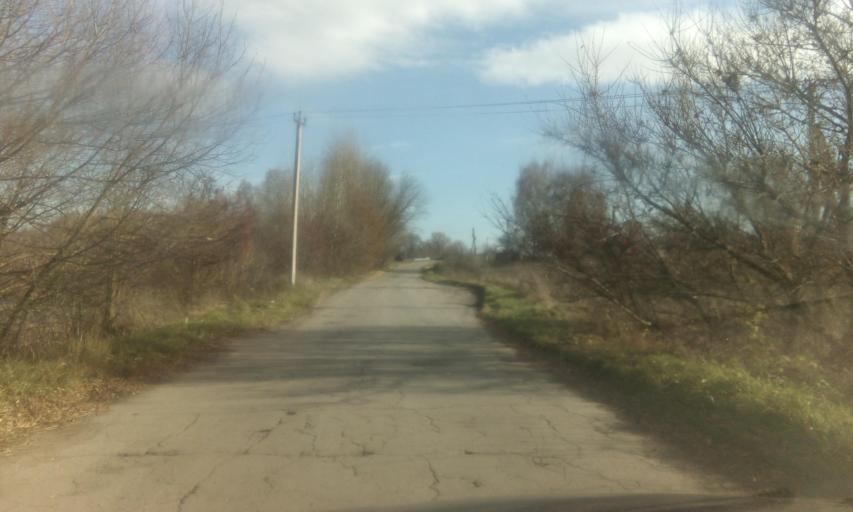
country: RU
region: Tula
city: Dubovka
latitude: 53.9465
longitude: 38.0309
